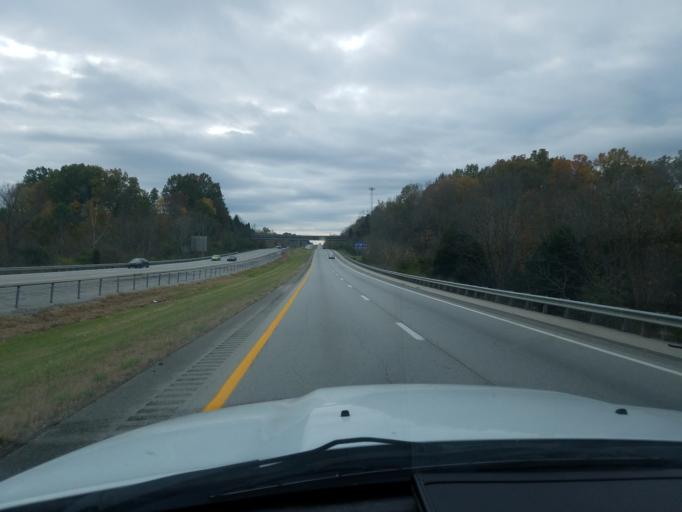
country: US
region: Kentucky
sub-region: Jefferson County
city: Middletown
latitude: 38.2086
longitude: -85.5071
